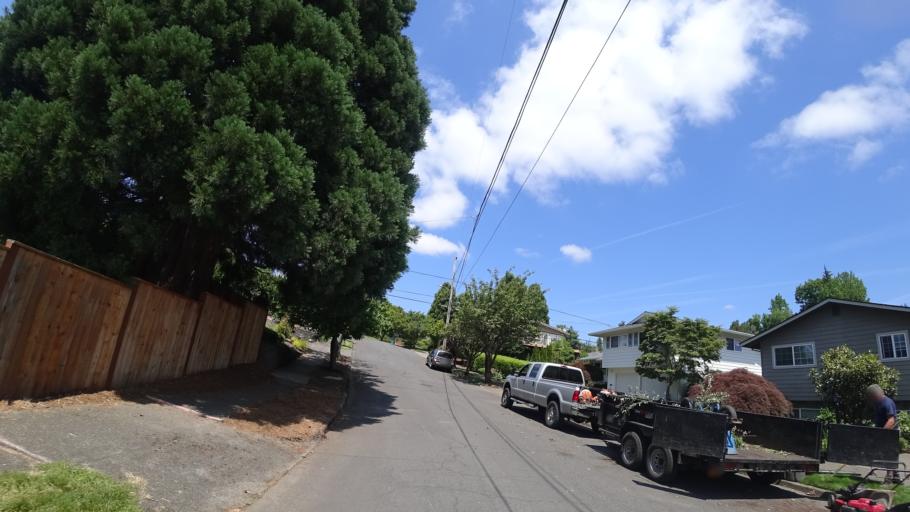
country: US
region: Oregon
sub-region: Multnomah County
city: Portland
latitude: 45.4721
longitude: -122.6914
